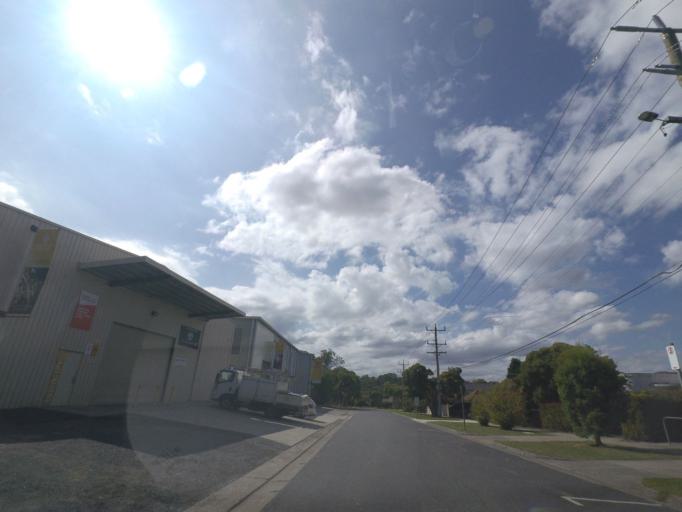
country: AU
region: Victoria
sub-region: Maroondah
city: Ringwood East
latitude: -37.8172
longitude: 145.2411
